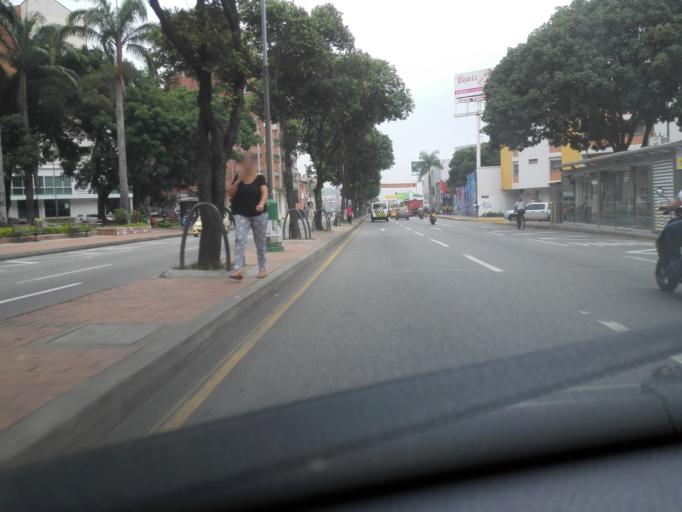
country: CO
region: Santander
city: Bucaramanga
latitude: 7.1154
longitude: -73.1152
